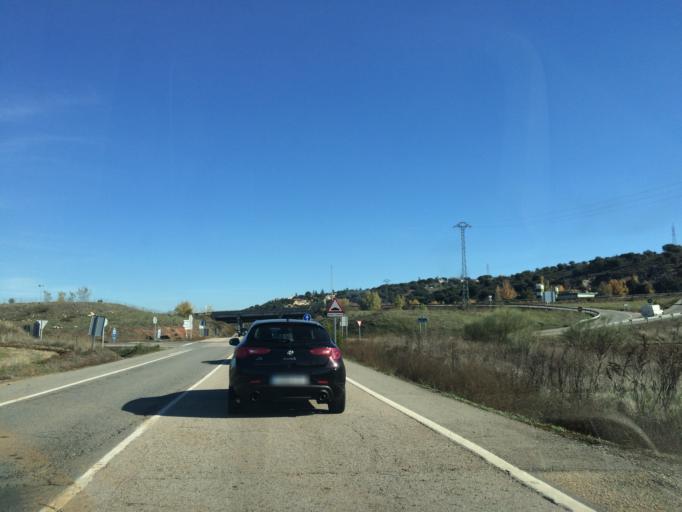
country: ES
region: Madrid
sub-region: Provincia de Madrid
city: Venturada
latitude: 40.7911
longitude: -3.6201
